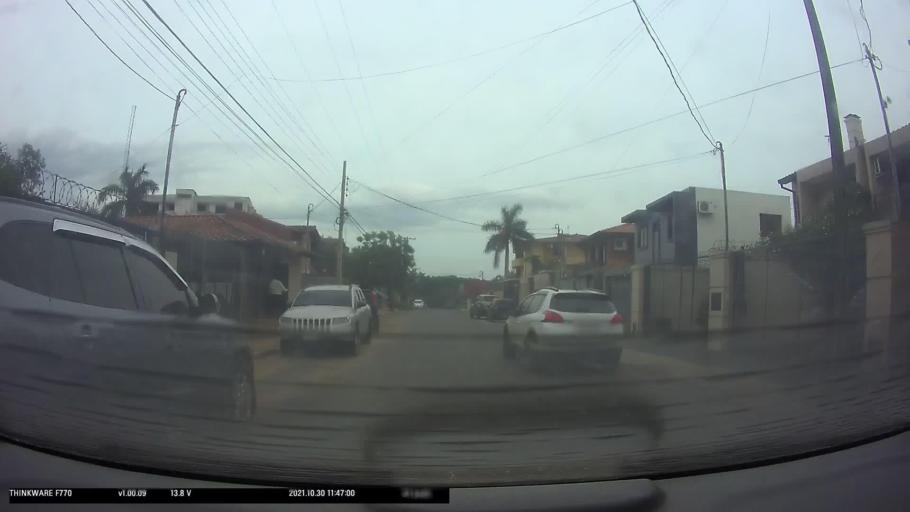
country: PY
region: Central
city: Fernando de la Mora
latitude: -25.3164
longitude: -57.5282
